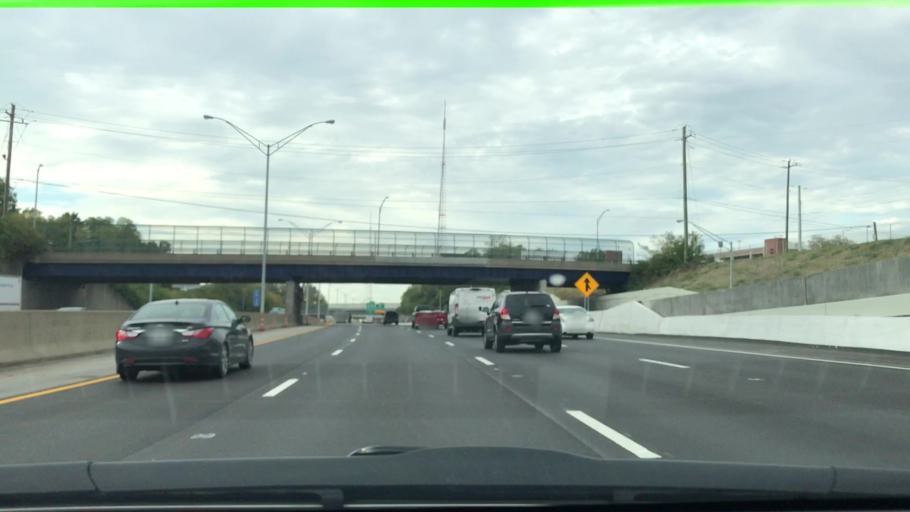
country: US
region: Kentucky
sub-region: Campbell County
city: Dayton
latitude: 39.1336
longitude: -84.4941
